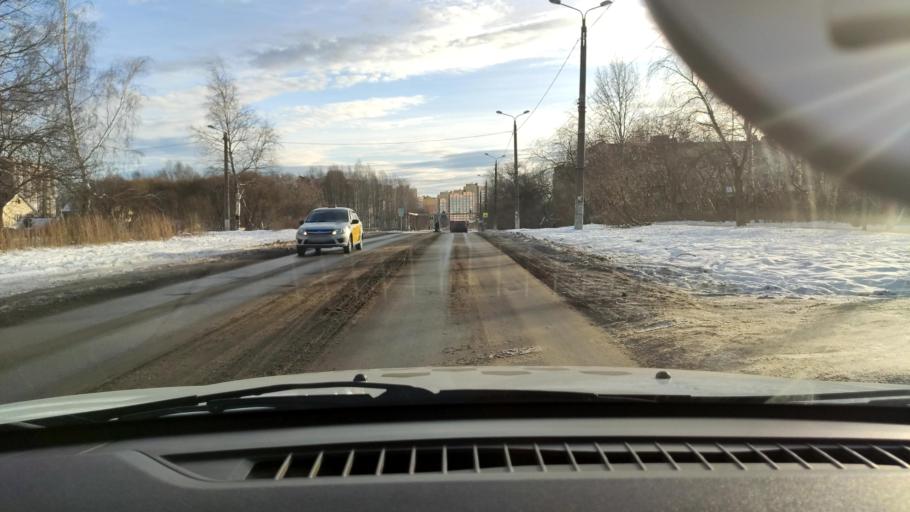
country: RU
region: Perm
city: Perm
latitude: 58.0874
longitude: 56.3948
